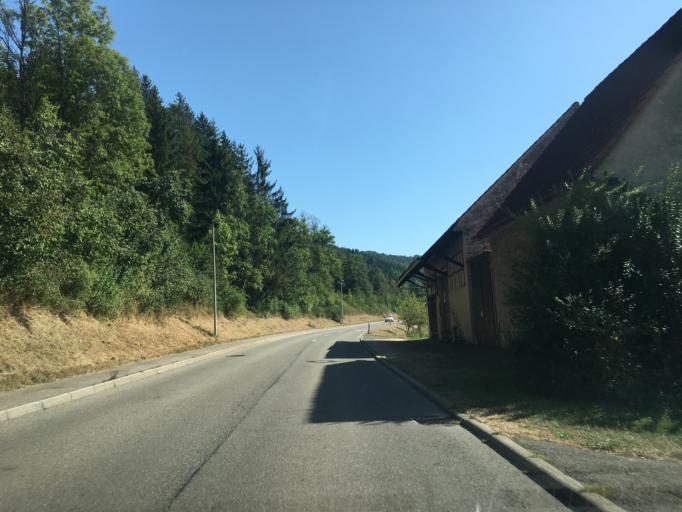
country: DE
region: Baden-Wuerttemberg
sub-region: Tuebingen Region
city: Munsingen
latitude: 48.3589
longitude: 9.4823
